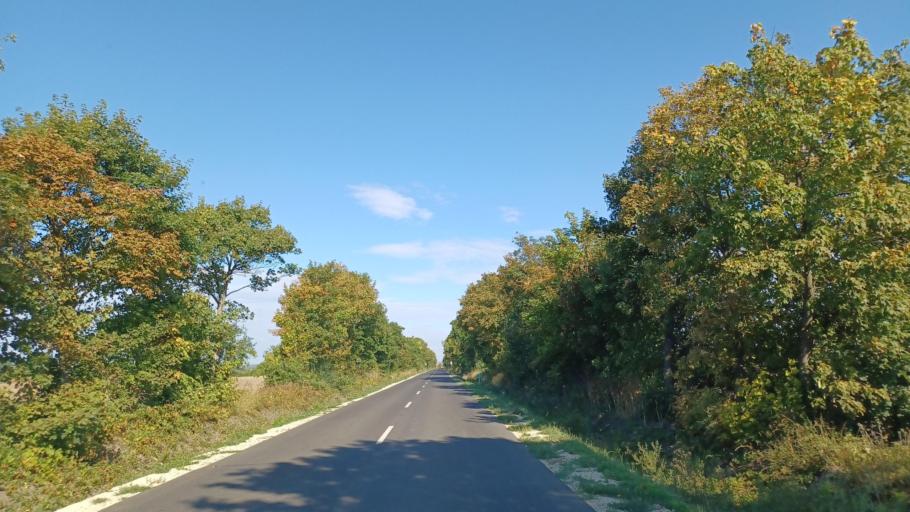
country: HU
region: Tolna
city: Dunaszentgyorgy
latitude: 46.4980
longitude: 18.8290
